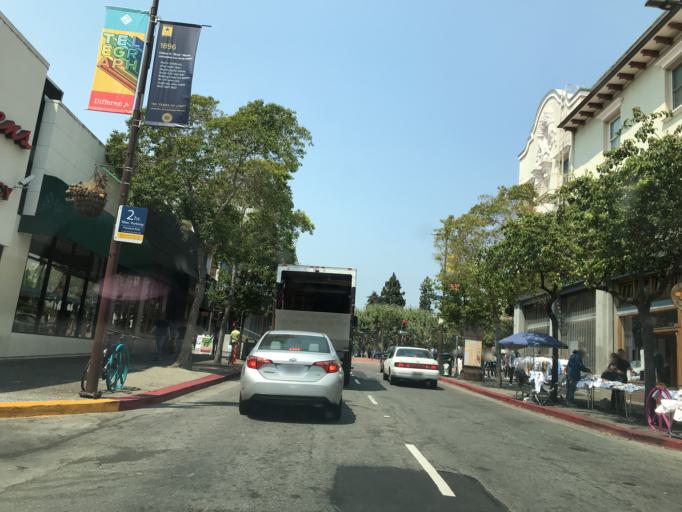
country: US
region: California
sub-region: Alameda County
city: Berkeley
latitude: 37.8683
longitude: -122.2591
